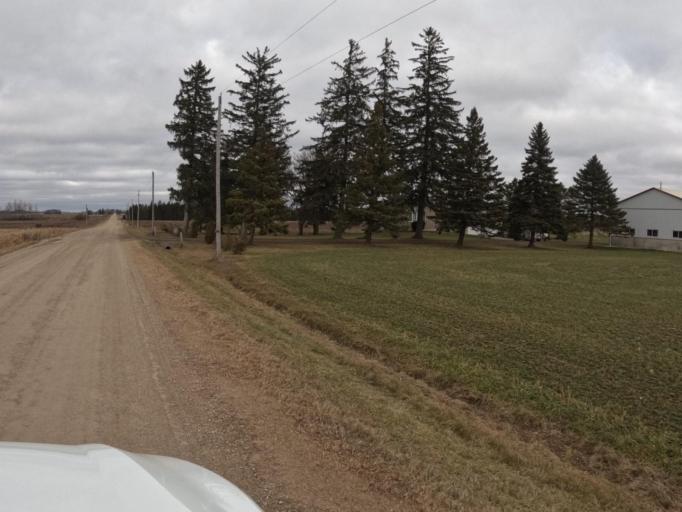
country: CA
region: Ontario
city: Shelburne
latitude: 43.8641
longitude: -80.4005
